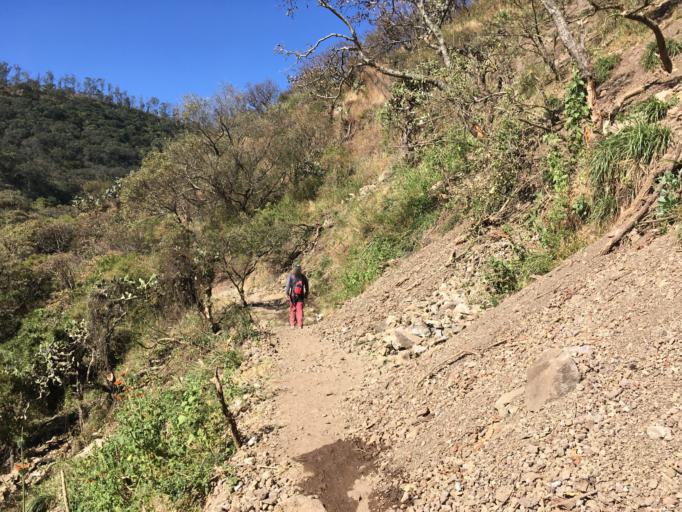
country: MX
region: Michoacan
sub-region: Morelia
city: Montana Monarca (Punta Altozano)
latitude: 19.6749
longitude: -101.1496
